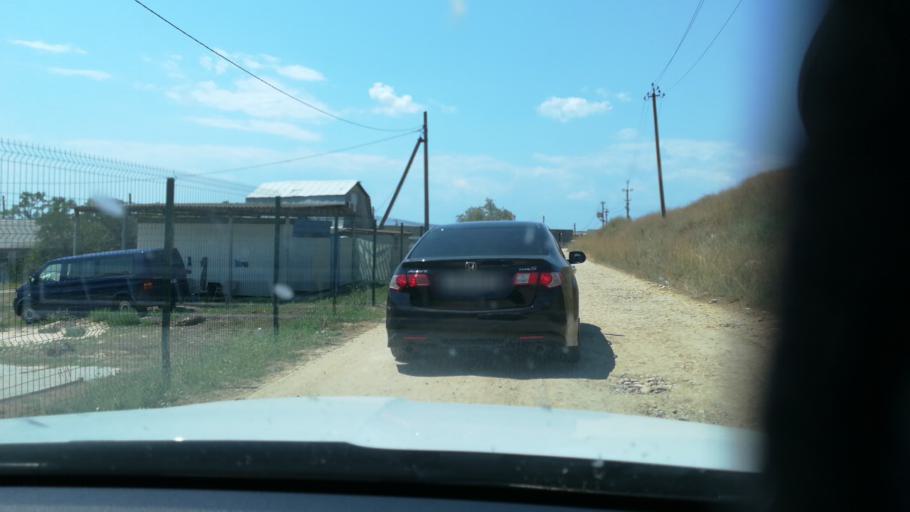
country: RU
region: Krasnodarskiy
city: Vyshestebliyevskaya
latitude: 45.1126
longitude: 36.8764
